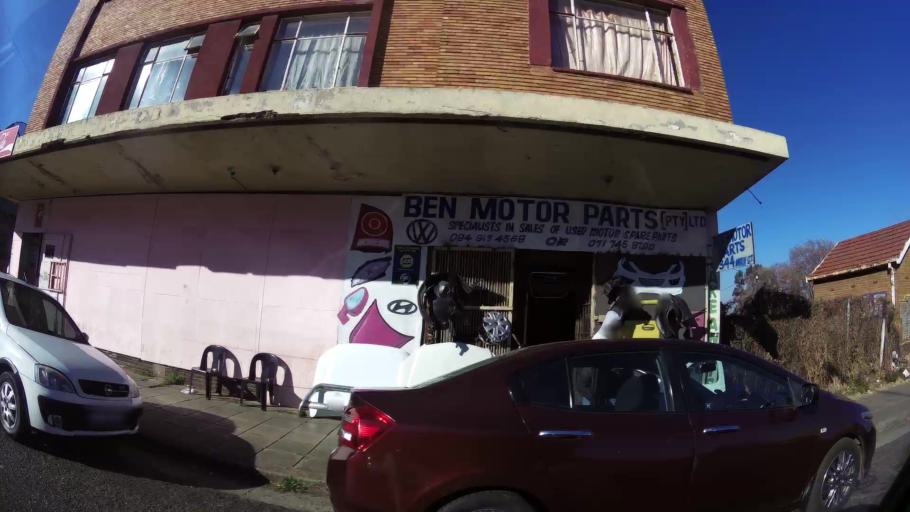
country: ZA
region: Gauteng
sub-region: City of Johannesburg Metropolitan Municipality
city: Johannesburg
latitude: -26.2040
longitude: 28.0669
